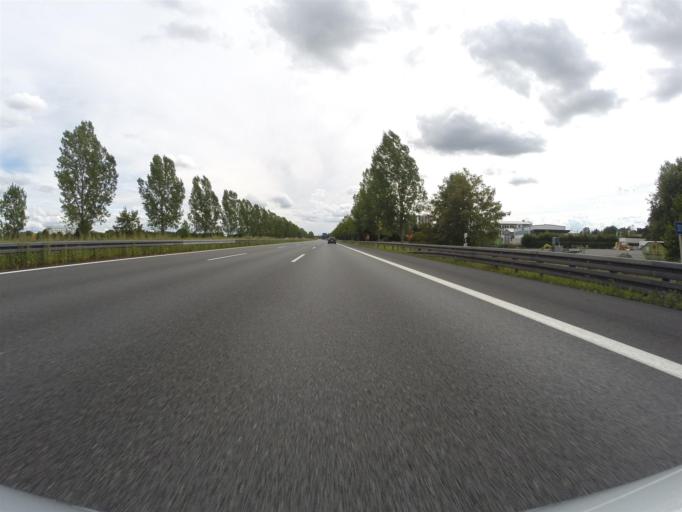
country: DE
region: Bavaria
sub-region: Upper Franconia
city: Bindlach
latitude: 49.9745
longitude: 11.6062
